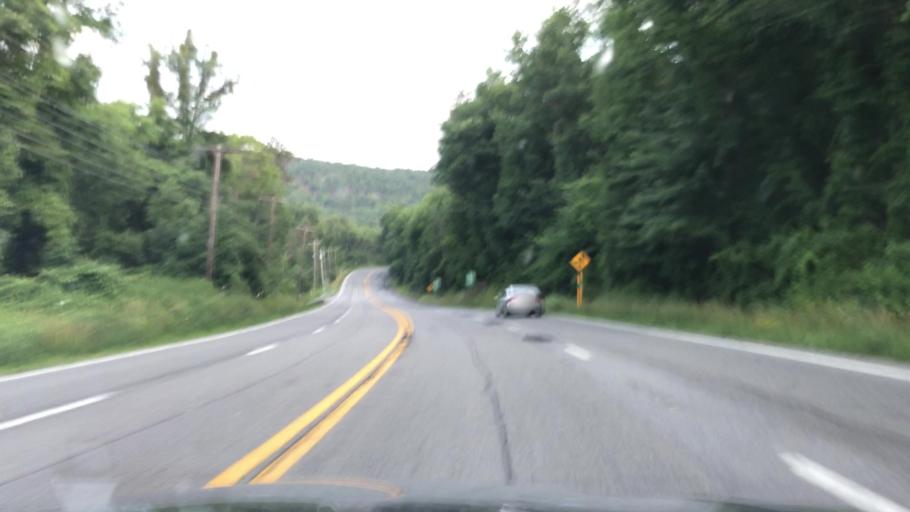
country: US
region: New York
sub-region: Orange County
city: Harriman
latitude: 41.2946
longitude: -74.1438
